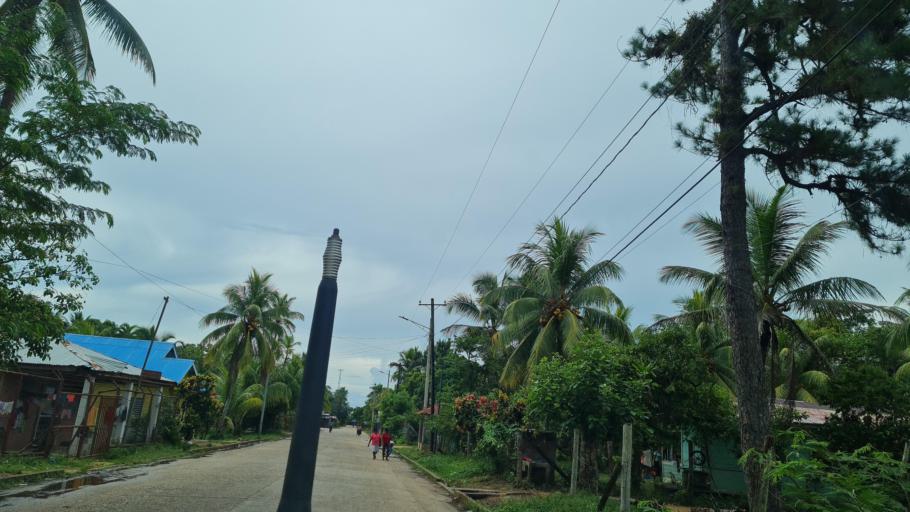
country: NI
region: Atlantico Norte (RAAN)
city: Waspam
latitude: 14.7344
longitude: -83.9692
